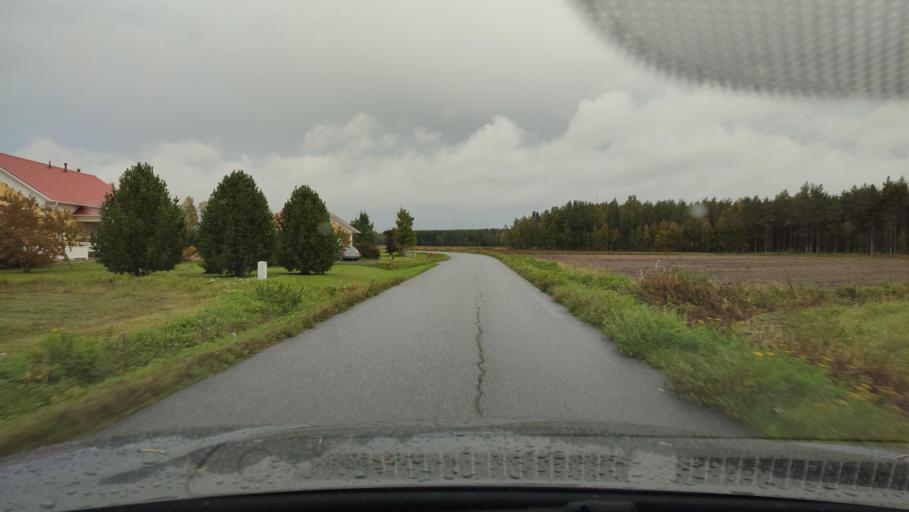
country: FI
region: Southern Ostrobothnia
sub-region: Suupohja
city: Karijoki
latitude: 62.2241
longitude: 21.6358
